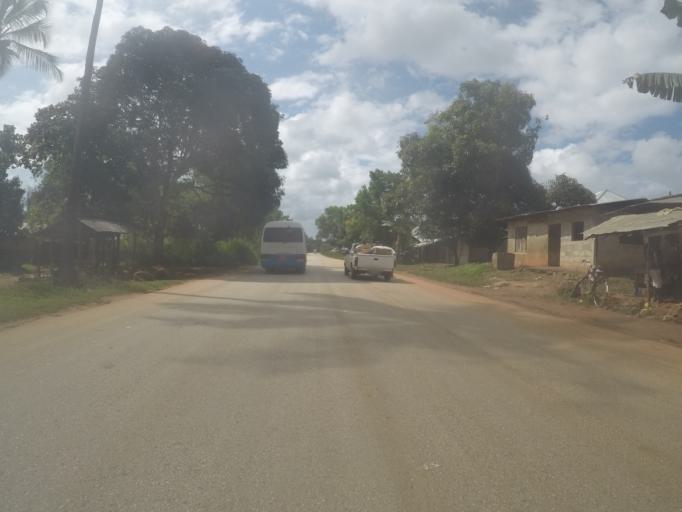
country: TZ
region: Zanzibar North
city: Mkokotoni
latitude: -5.8648
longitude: 39.2808
